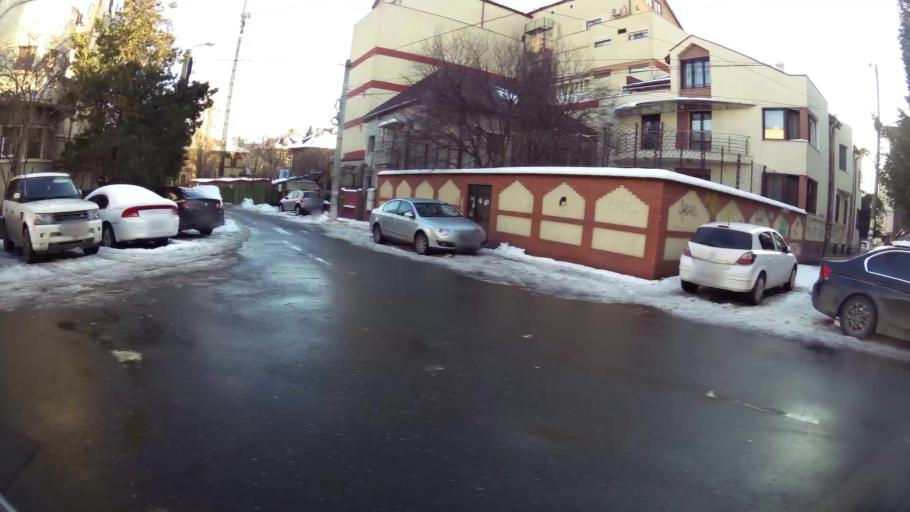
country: RO
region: Bucuresti
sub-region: Municipiul Bucuresti
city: Bucuresti
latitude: 44.4315
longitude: 26.0719
